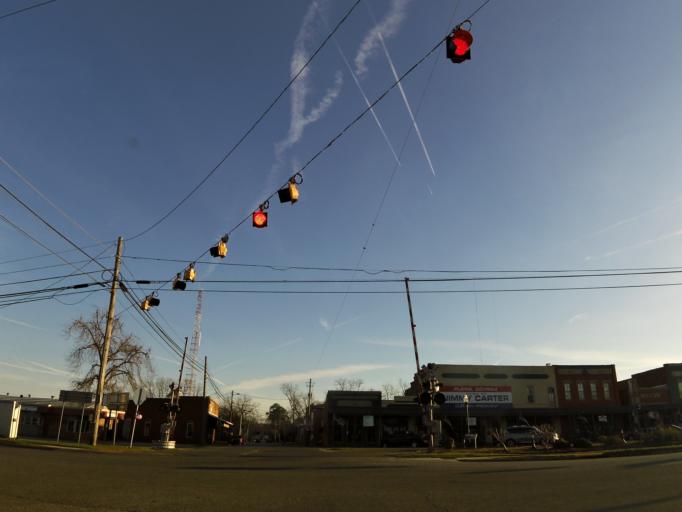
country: US
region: Georgia
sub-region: Webster County
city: Preston
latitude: 32.0341
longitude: -84.3928
